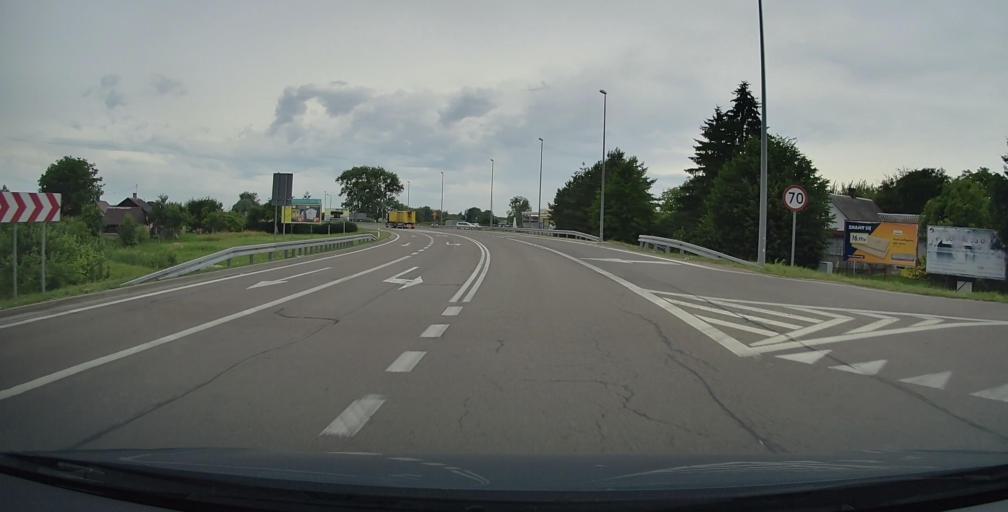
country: PL
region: Lublin Voivodeship
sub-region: Powiat bialski
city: Terespol
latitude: 52.0624
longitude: 23.5858
